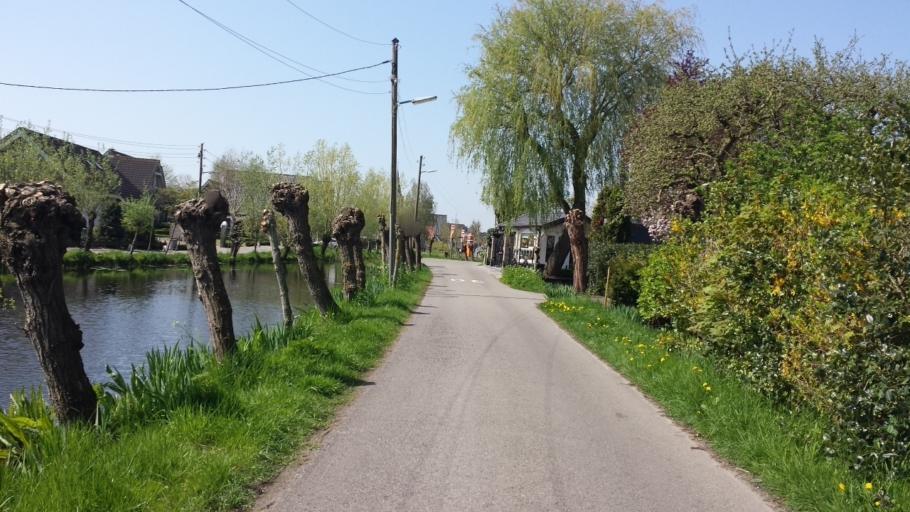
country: NL
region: South Holland
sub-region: Gemeente Vlist
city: Haastrecht
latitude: 51.9732
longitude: 4.7768
